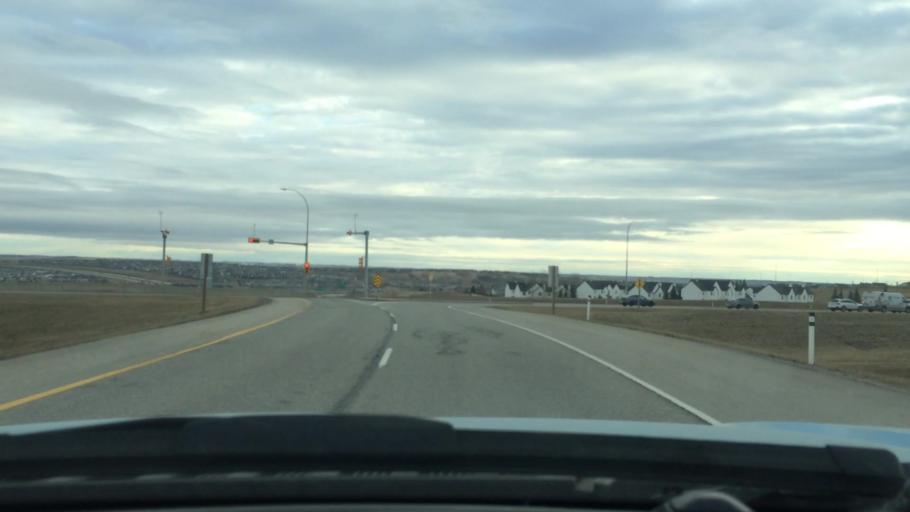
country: CA
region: Alberta
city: Calgary
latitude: 51.1504
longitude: -114.1408
